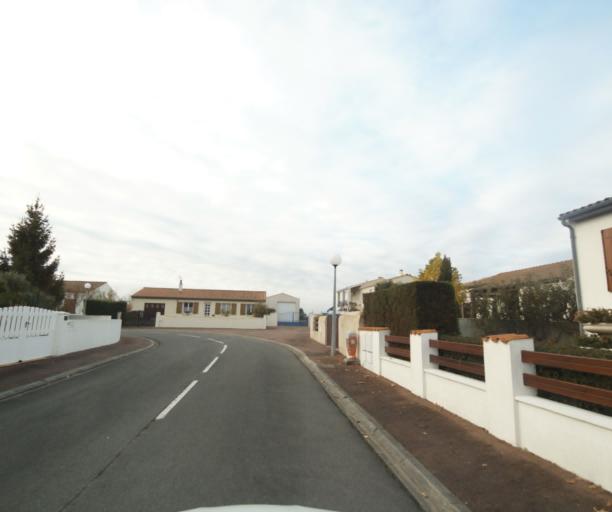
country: FR
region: Poitou-Charentes
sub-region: Departement de la Charente-Maritime
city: Saintes
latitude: 45.7503
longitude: -0.6506
